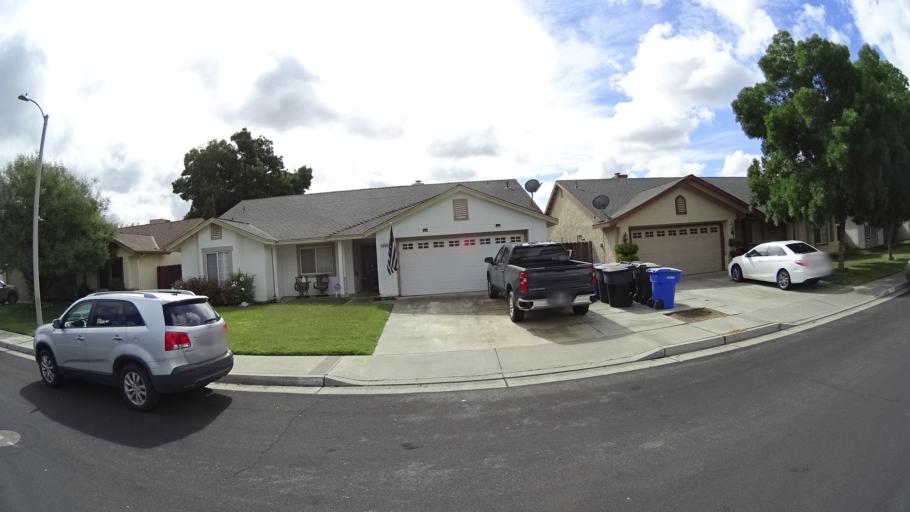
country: US
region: California
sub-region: Kings County
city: Lucerne
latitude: 36.3633
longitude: -119.6506
